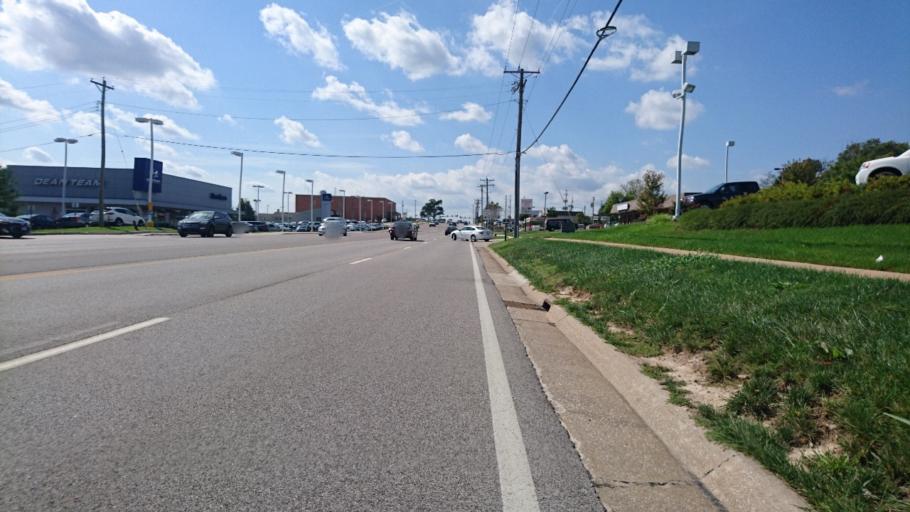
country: US
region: Missouri
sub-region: Saint Louis County
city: Winchester
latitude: 38.5931
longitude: -90.5328
